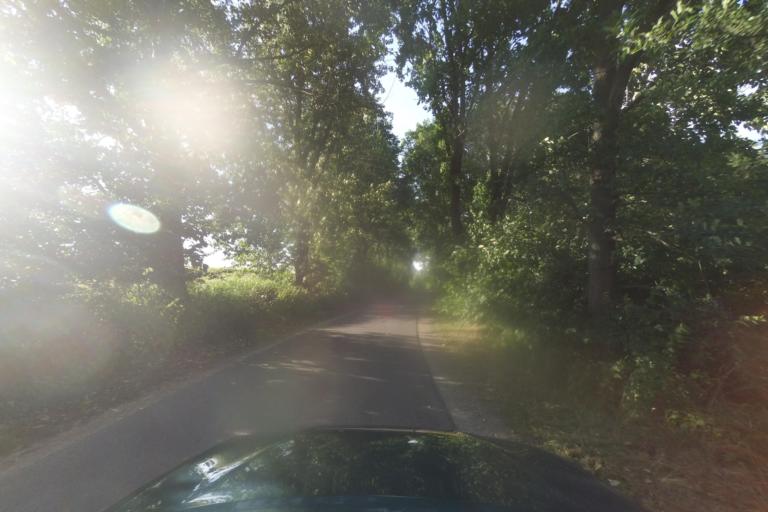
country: PL
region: Lower Silesian Voivodeship
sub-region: Powiat dzierzoniowski
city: Niemcza
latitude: 50.6992
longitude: 16.8421
